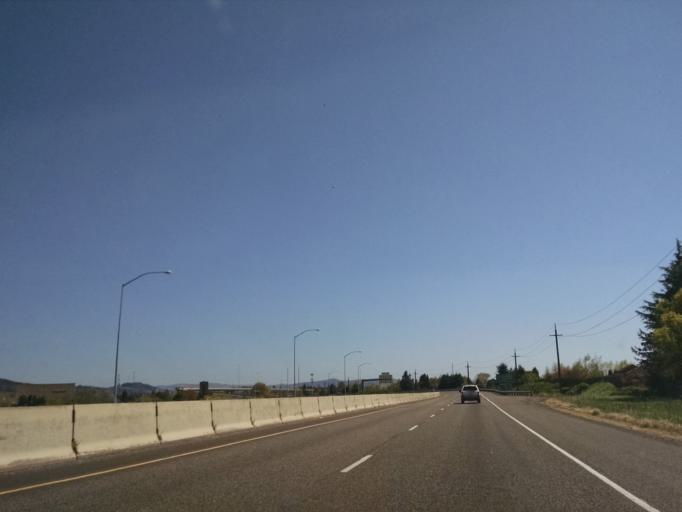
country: US
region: Oregon
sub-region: Lane County
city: Eugene
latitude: 44.0857
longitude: -123.0597
